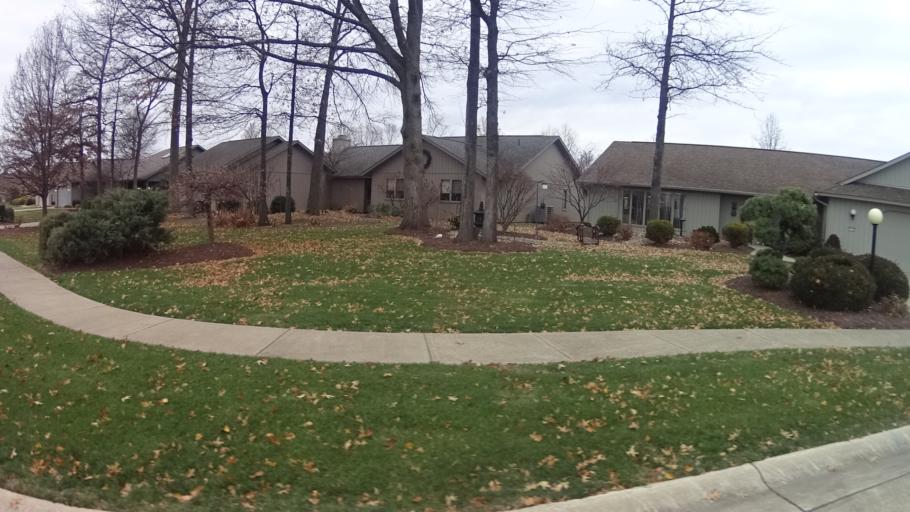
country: US
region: Ohio
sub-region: Lorain County
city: North Ridgeville
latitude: 41.3651
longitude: -81.9823
